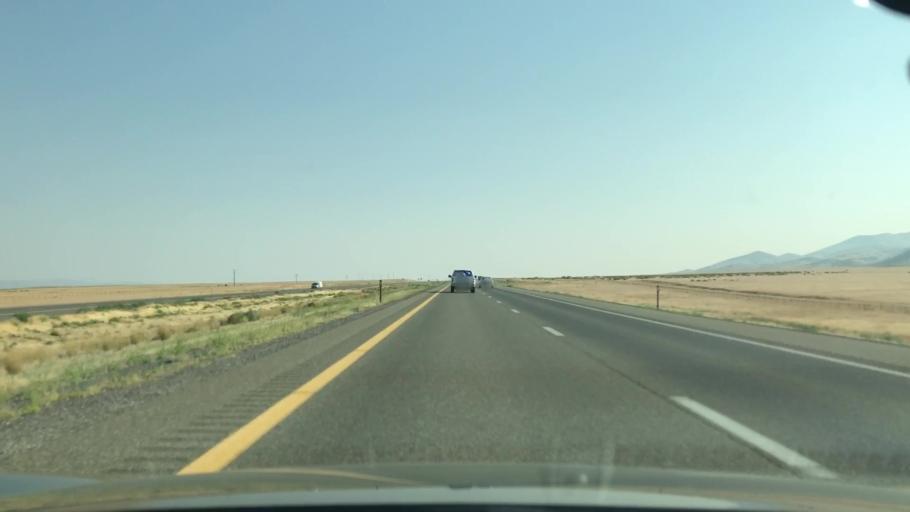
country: US
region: Nevada
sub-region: Humboldt County
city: Winnemucca
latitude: 40.7721
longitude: -118.0088
